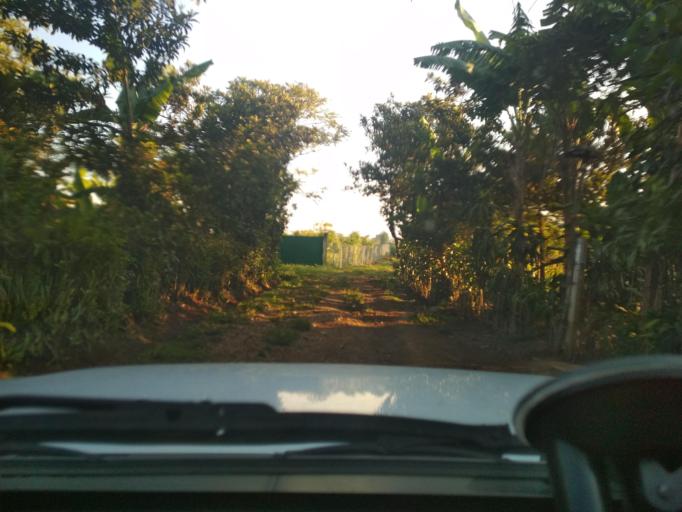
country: MX
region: Veracruz
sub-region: Fortin
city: Fraccionamiento Villas de la Llave
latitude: 18.9225
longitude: -97.0003
